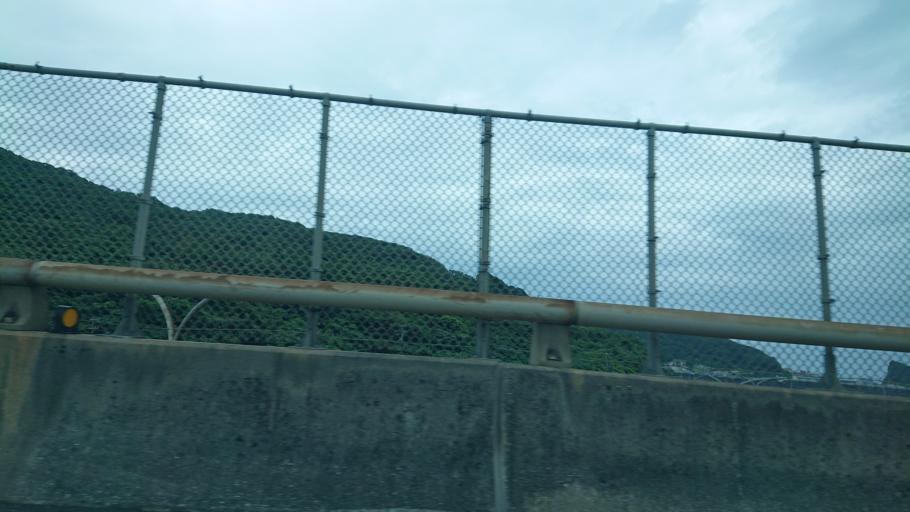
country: TW
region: Taiwan
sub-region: Keelung
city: Keelung
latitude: 25.1224
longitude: 121.8193
